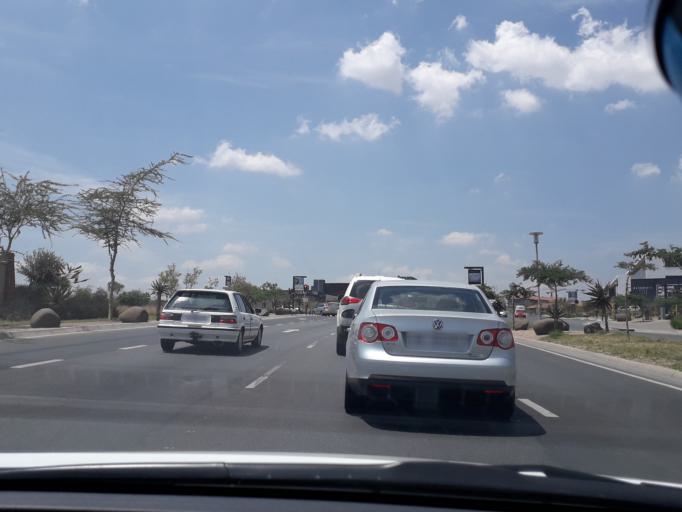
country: ZA
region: Gauteng
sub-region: City of Johannesburg Metropolitan Municipality
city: Midrand
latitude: -26.0145
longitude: 28.0949
